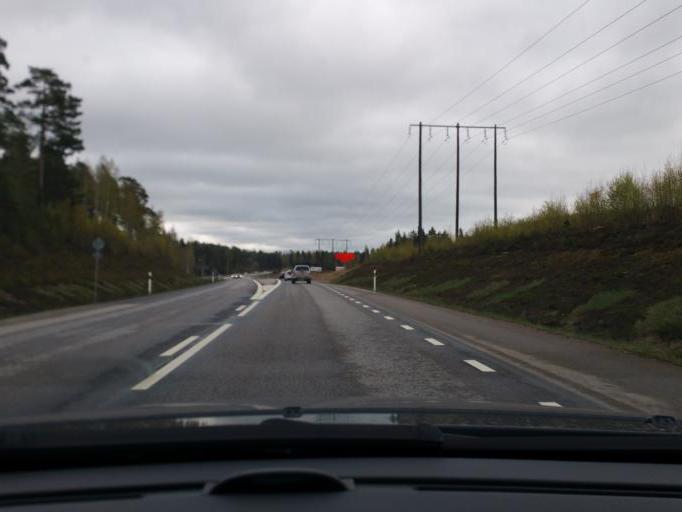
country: SE
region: Kronoberg
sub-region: Vaxjo Kommun
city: Vaexjoe
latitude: 56.8642
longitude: 14.8447
